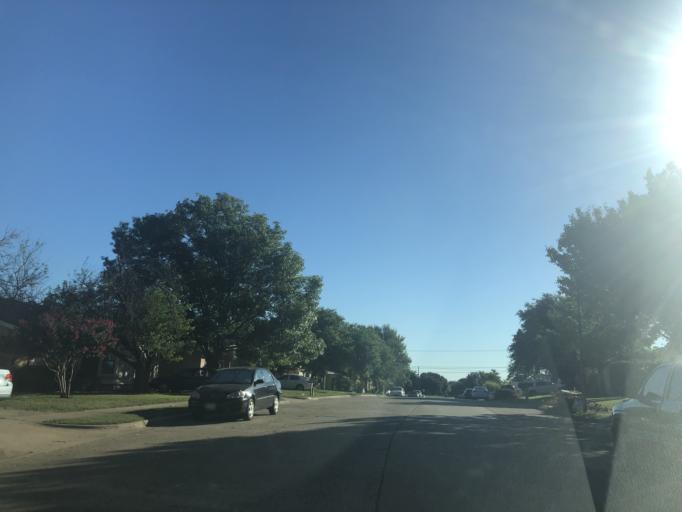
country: US
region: Texas
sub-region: Dallas County
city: Cedar Hill
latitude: 32.6347
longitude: -96.9538
